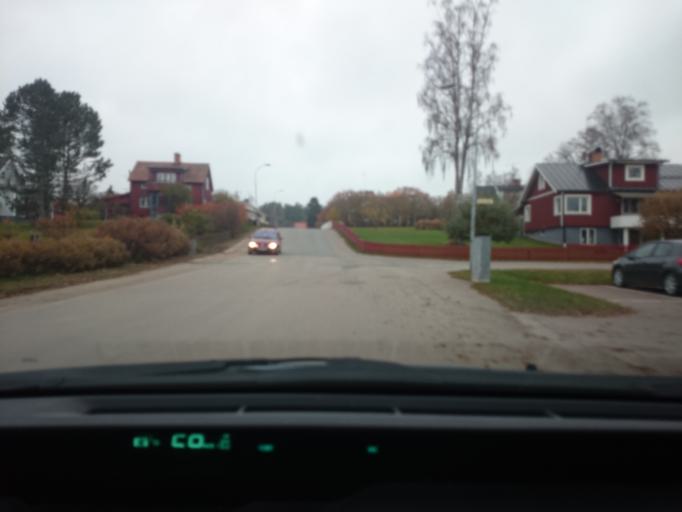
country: SE
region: Dalarna
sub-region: Saters Kommun
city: Saeter
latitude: 60.3522
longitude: 15.7438
